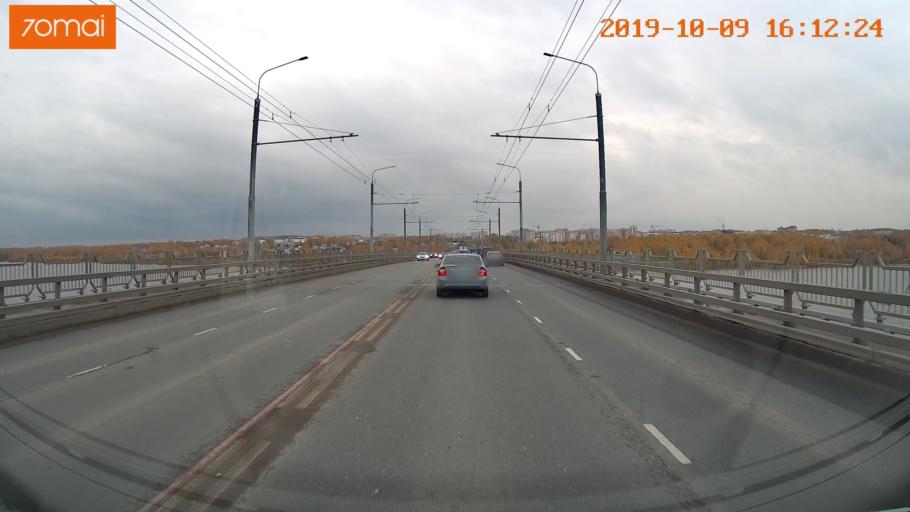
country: RU
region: Kostroma
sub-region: Kostromskoy Rayon
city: Kostroma
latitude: 57.7520
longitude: 40.9379
